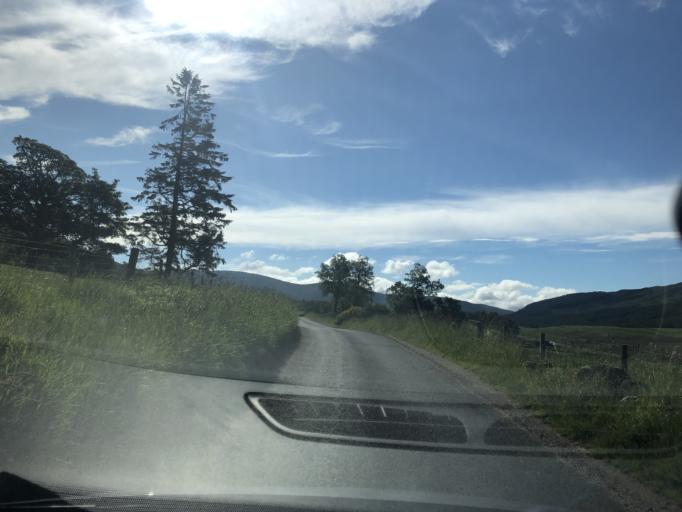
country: GB
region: Scotland
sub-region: Angus
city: Kirriemuir
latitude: 56.8433
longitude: -3.1013
